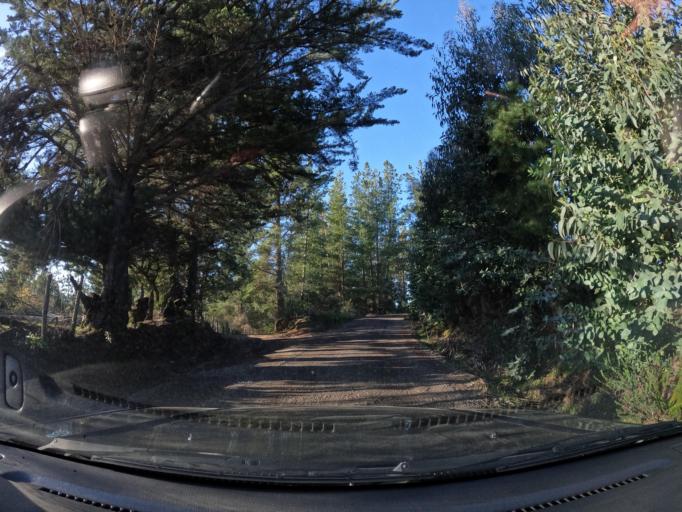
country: CL
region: Biobio
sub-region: Provincia de Concepcion
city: Chiguayante
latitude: -37.0134
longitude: -72.8474
